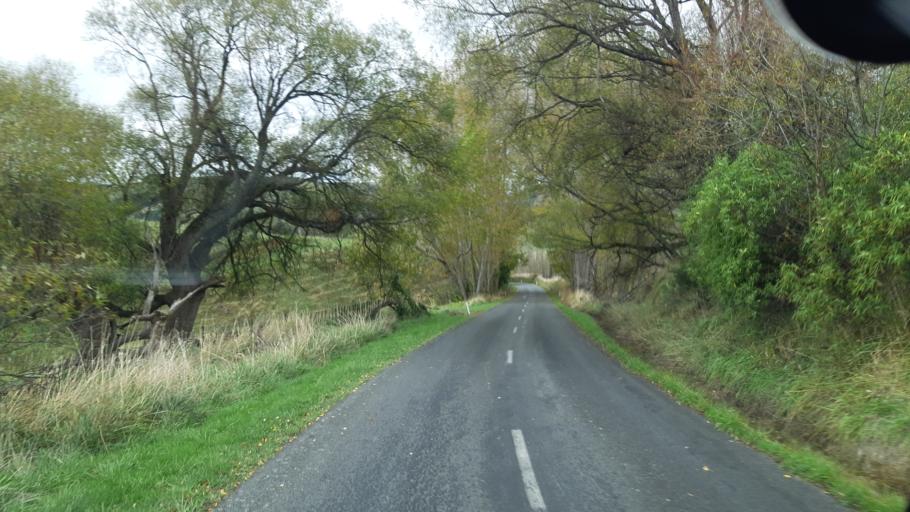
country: NZ
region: Manawatu-Wanganui
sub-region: Ruapehu District
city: Waiouru
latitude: -39.6123
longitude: 175.6686
